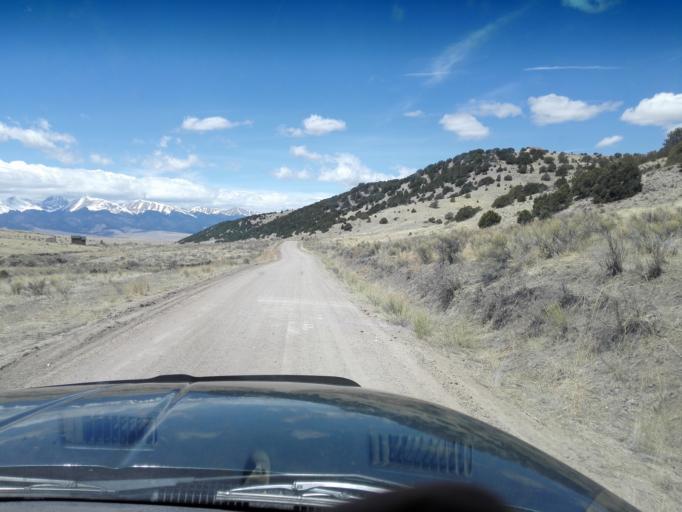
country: US
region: Colorado
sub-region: Custer County
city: Westcliffe
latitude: 37.9730
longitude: -105.2680
